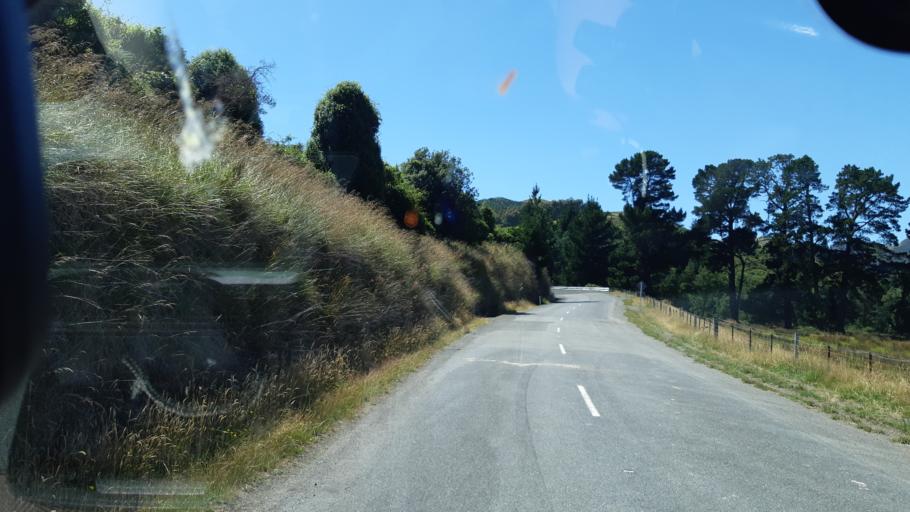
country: NZ
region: Canterbury
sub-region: Kaikoura District
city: Kaikoura
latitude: -42.6594
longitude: 173.3244
